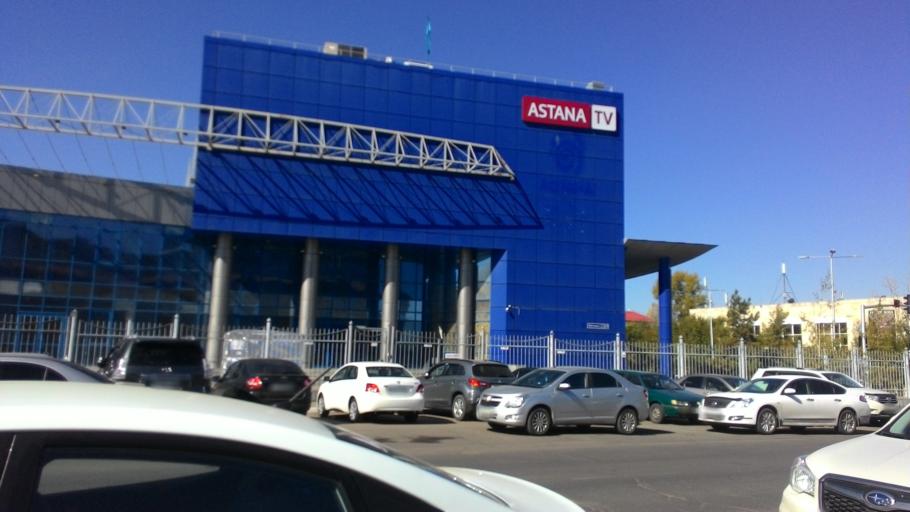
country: KZ
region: Astana Qalasy
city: Astana
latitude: 51.1813
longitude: 71.4121
